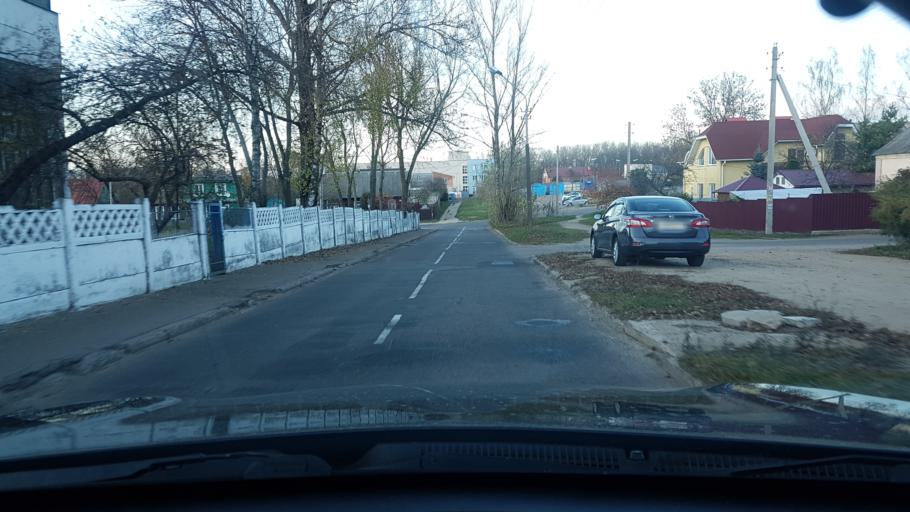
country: BY
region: Minsk
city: Minsk
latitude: 53.9353
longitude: 27.5415
